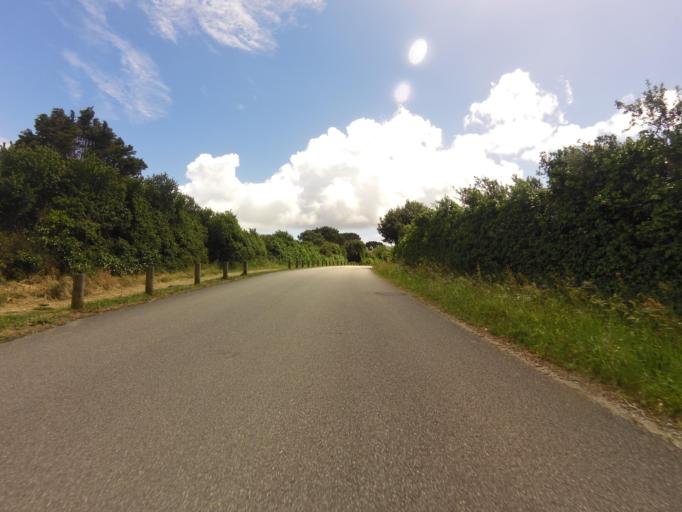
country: FR
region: Brittany
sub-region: Departement du Morbihan
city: Locmariaquer
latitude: 47.5574
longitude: -2.9304
